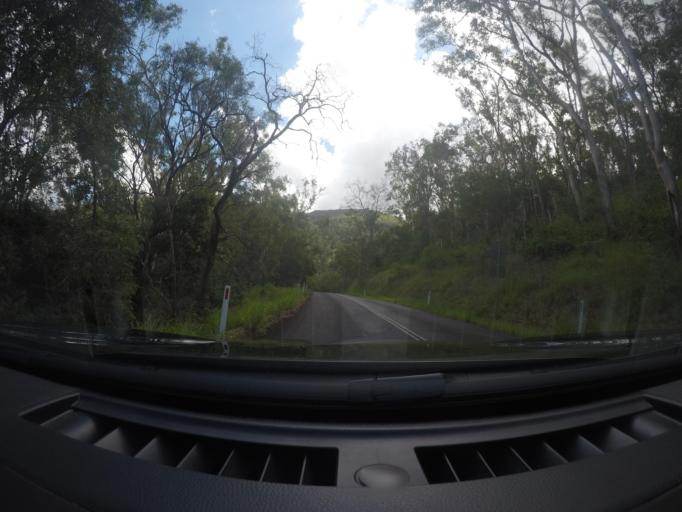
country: AU
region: Queensland
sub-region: Moreton Bay
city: Woodford
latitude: -27.1005
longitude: 152.5610
